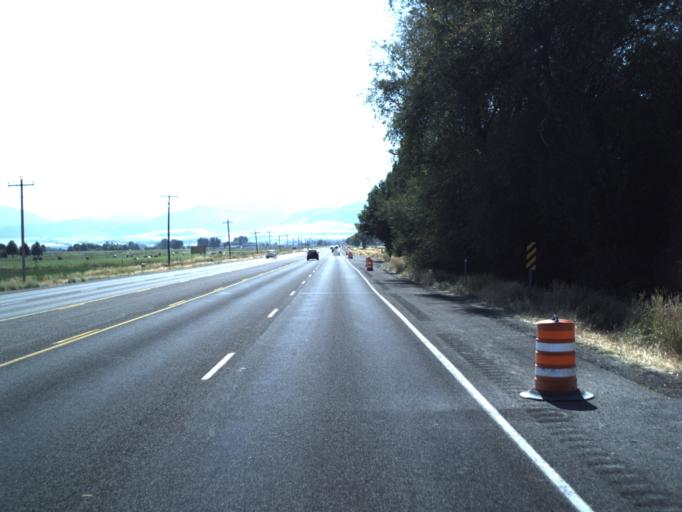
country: US
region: Utah
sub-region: Cache County
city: Wellsville
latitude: 41.6595
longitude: -111.8993
